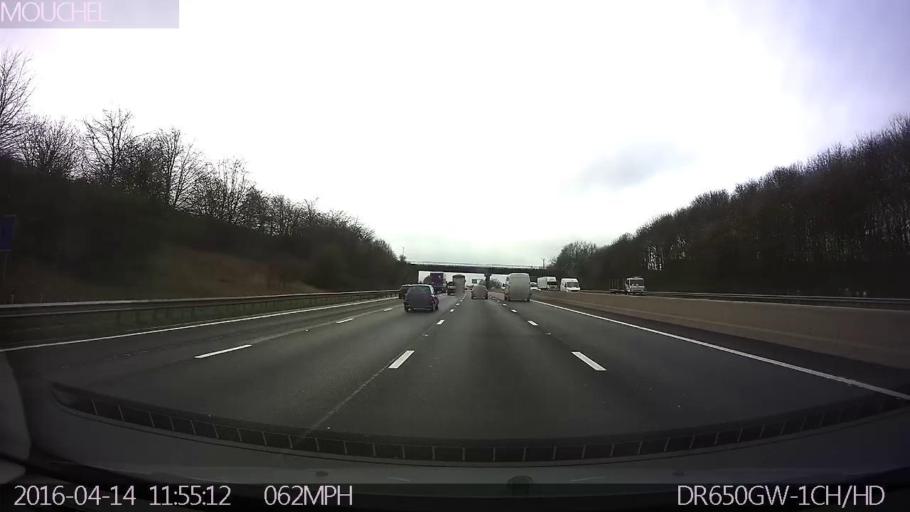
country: GB
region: England
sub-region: Derbyshire
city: Tibshelf
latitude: 53.1486
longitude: -1.3295
